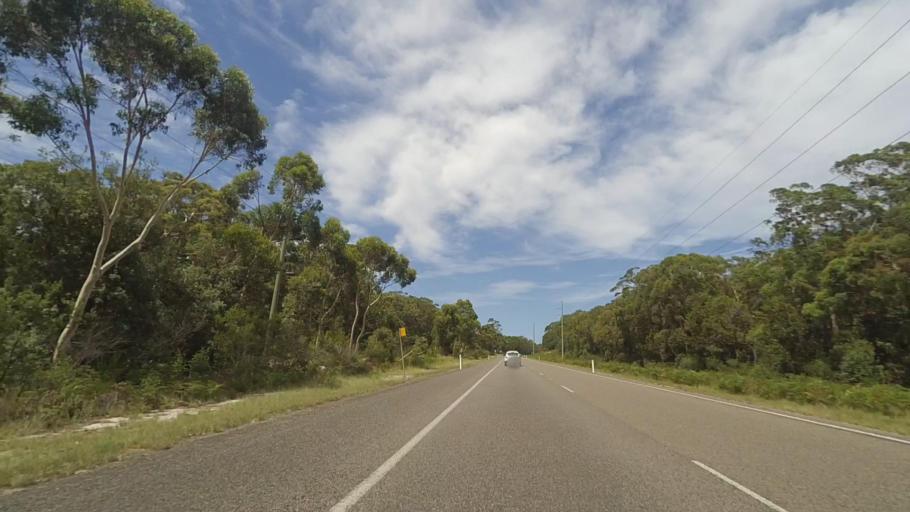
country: AU
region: New South Wales
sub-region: Port Stephens Shire
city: Medowie
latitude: -32.7878
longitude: 151.9634
